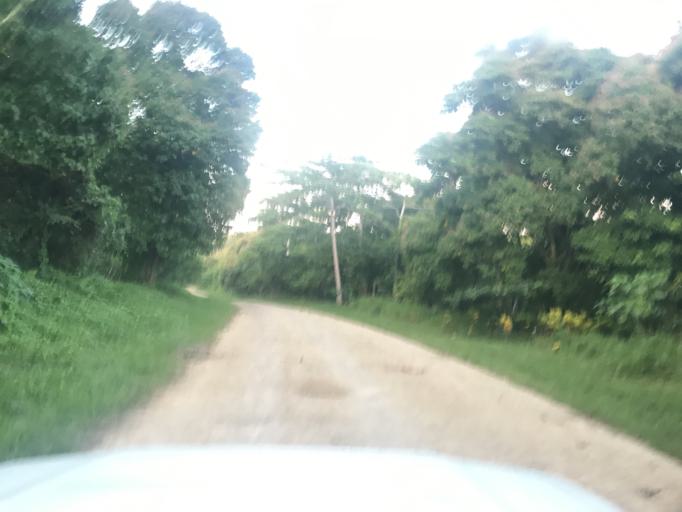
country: VU
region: Sanma
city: Luganville
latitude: -15.5603
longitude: 166.9643
